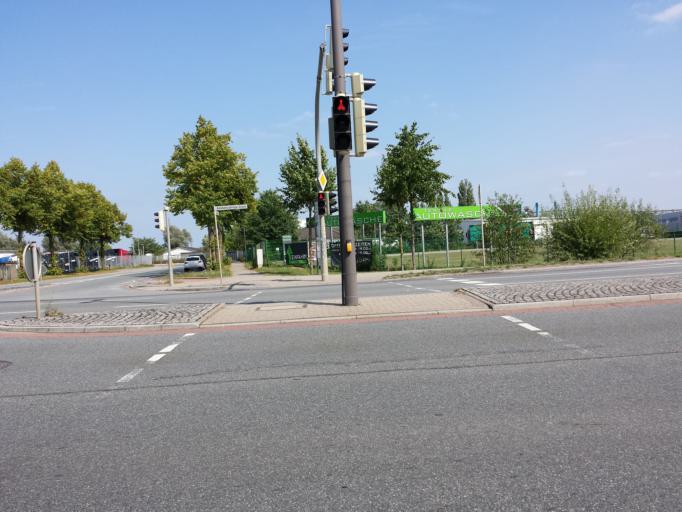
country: DE
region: Bremen
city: Bremen
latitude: 53.0231
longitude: 8.8651
